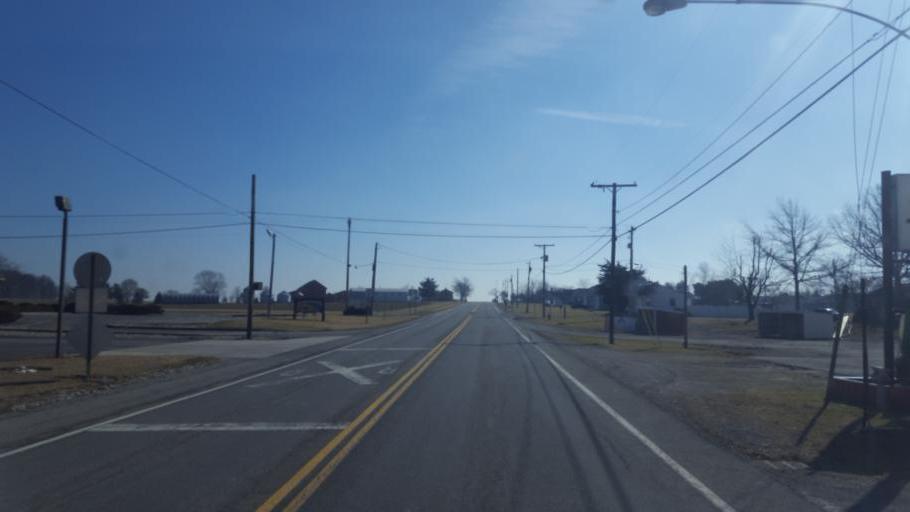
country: US
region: Ohio
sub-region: Huron County
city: Willard
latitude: 41.0625
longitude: -82.8809
